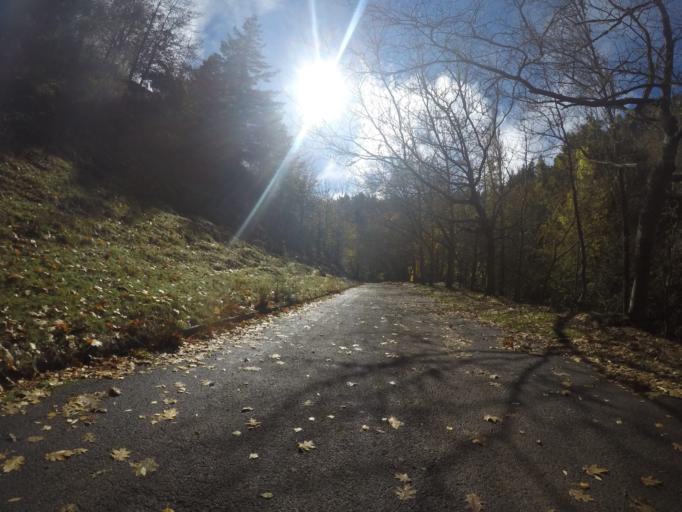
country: PT
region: Madeira
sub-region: Funchal
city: Nossa Senhora do Monte
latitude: 32.6987
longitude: -16.8819
